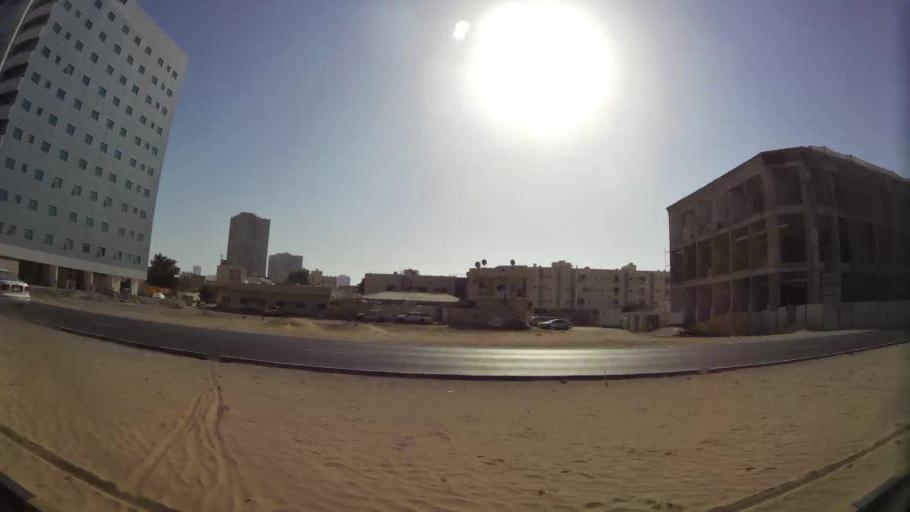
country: AE
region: Ajman
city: Ajman
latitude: 25.4062
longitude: 55.4516
